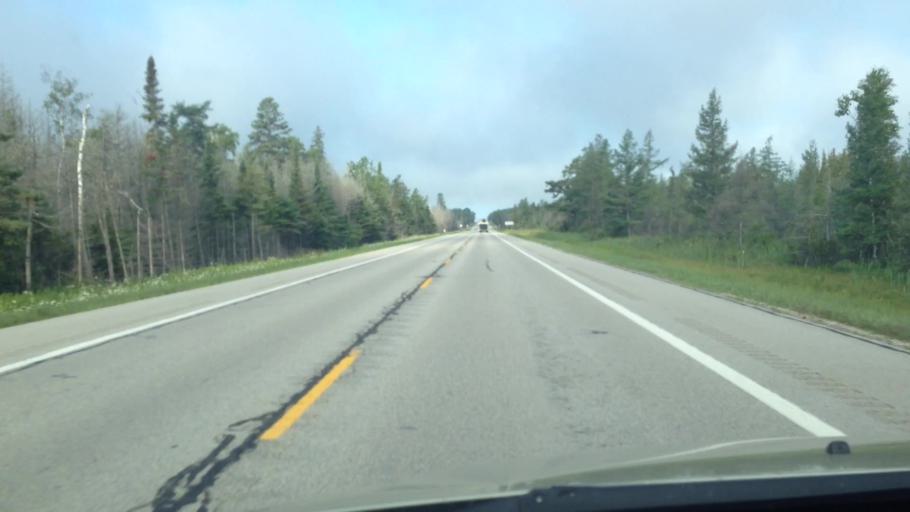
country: US
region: Michigan
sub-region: Luce County
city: Newberry
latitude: 46.1010
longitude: -85.5787
